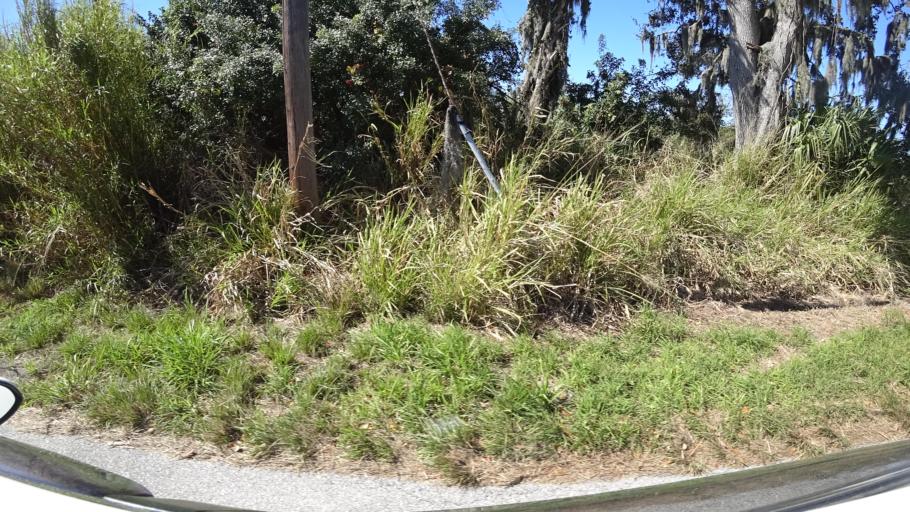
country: US
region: Florida
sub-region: Manatee County
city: Memphis
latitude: 27.5670
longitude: -82.5483
